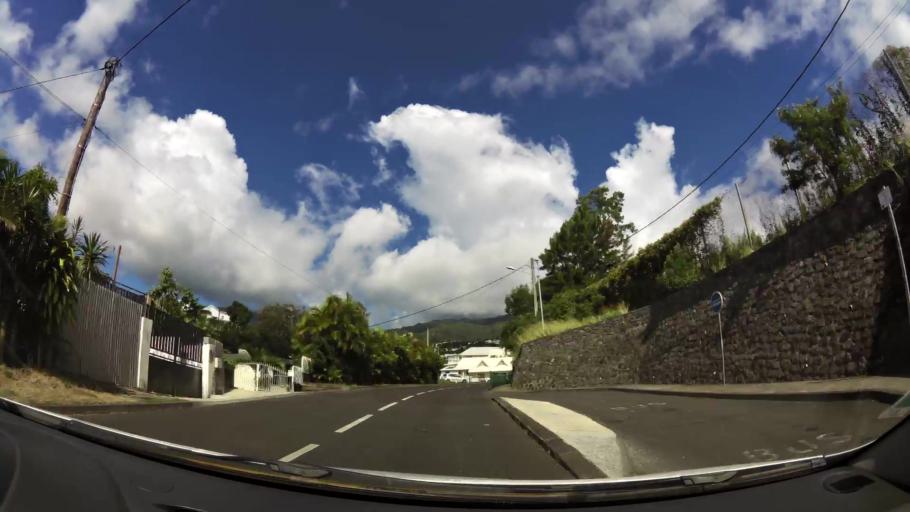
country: RE
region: Reunion
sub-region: Reunion
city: Saint-Denis
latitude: -20.9251
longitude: 55.4946
